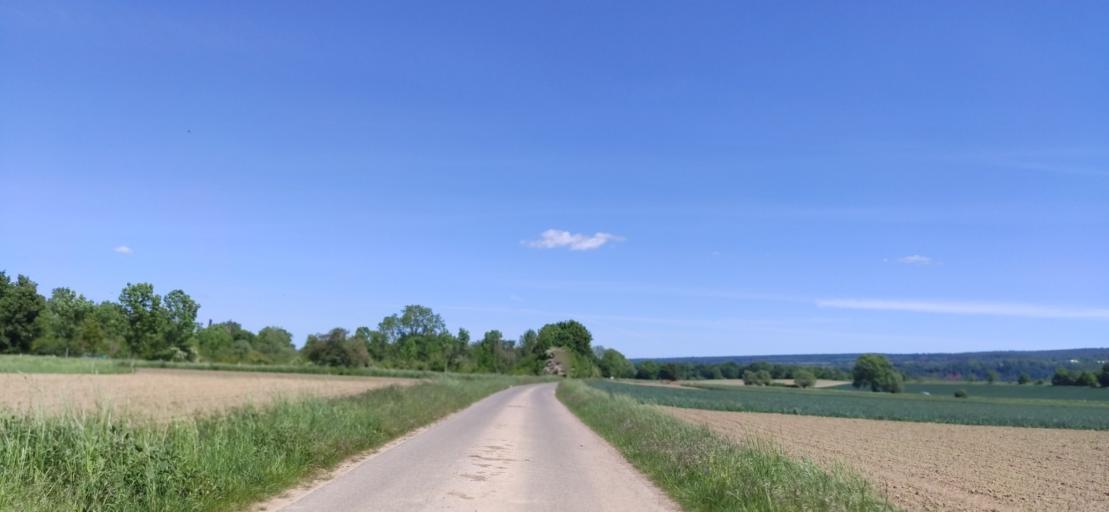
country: DE
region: Lower Saxony
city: Boffzen
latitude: 51.7237
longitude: 9.3647
